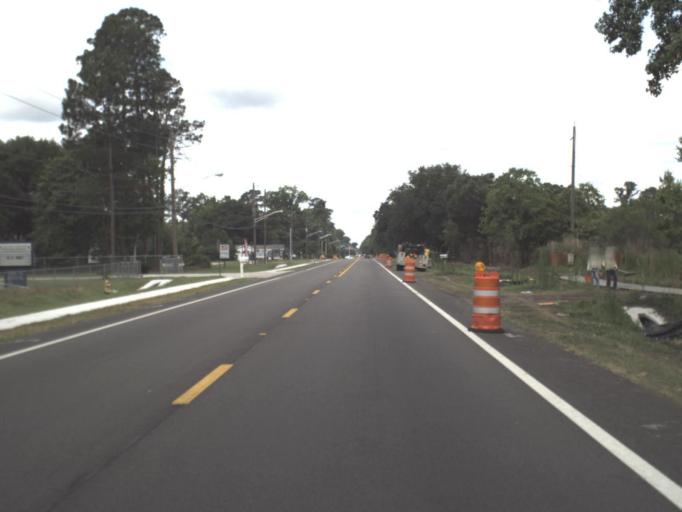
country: US
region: Florida
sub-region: Nassau County
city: Nassau Village-Ratliff
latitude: 30.4381
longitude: -81.7360
